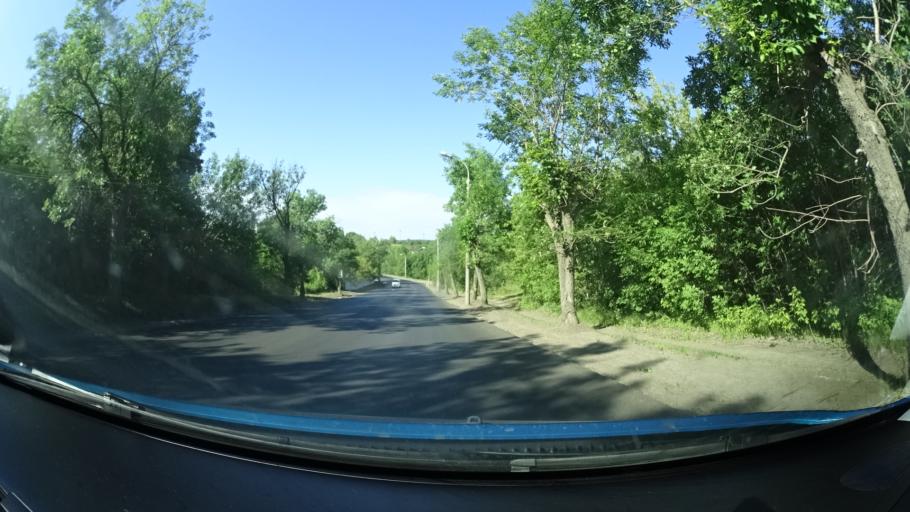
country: RU
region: Bashkortostan
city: Ufa
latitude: 54.8339
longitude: 56.0752
